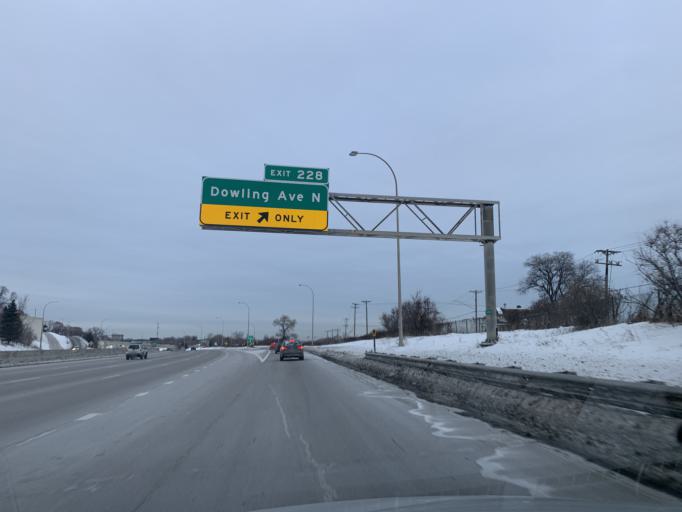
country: US
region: Minnesota
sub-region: Anoka County
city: Columbia Heights
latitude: 45.0188
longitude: -93.2823
